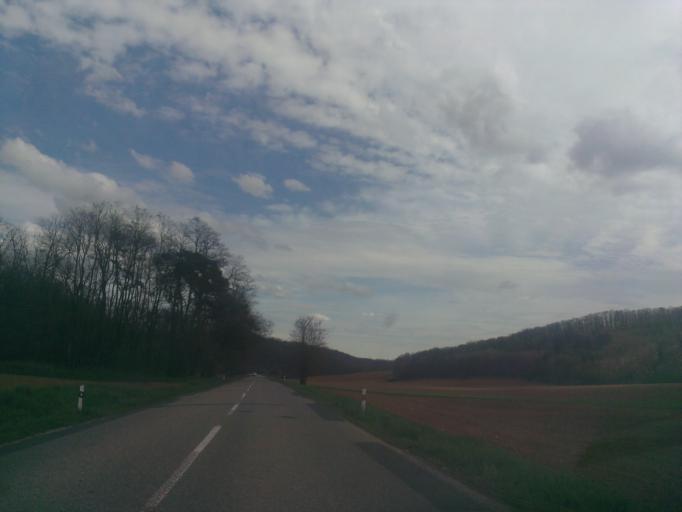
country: CZ
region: South Moravian
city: Dolni Kounice
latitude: 49.1023
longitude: 16.4523
